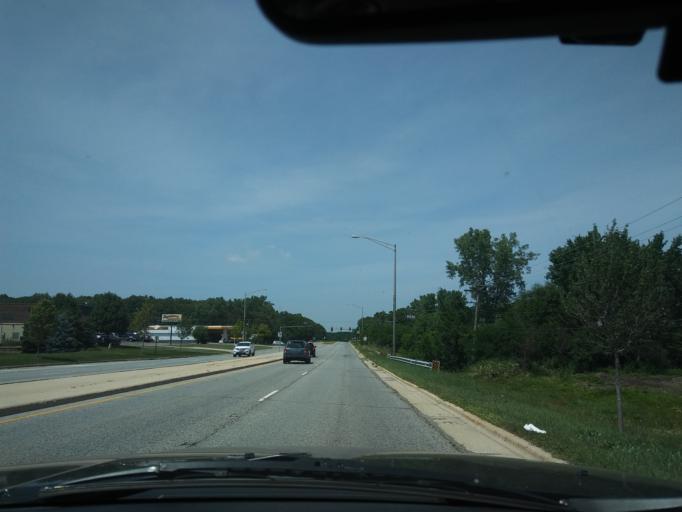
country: US
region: Illinois
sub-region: Cook County
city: Tinley Park
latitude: 41.6150
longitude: -87.7944
